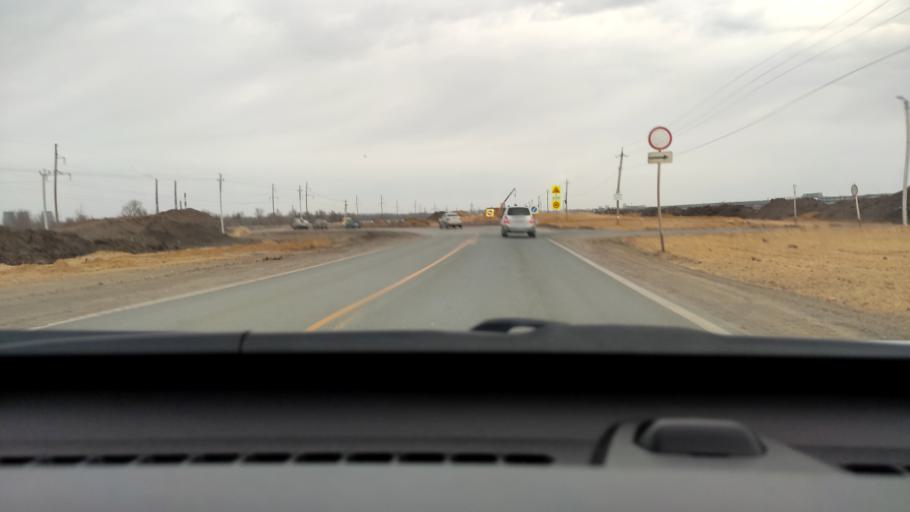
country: RU
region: Samara
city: Podstepki
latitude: 53.5622
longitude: 49.1776
